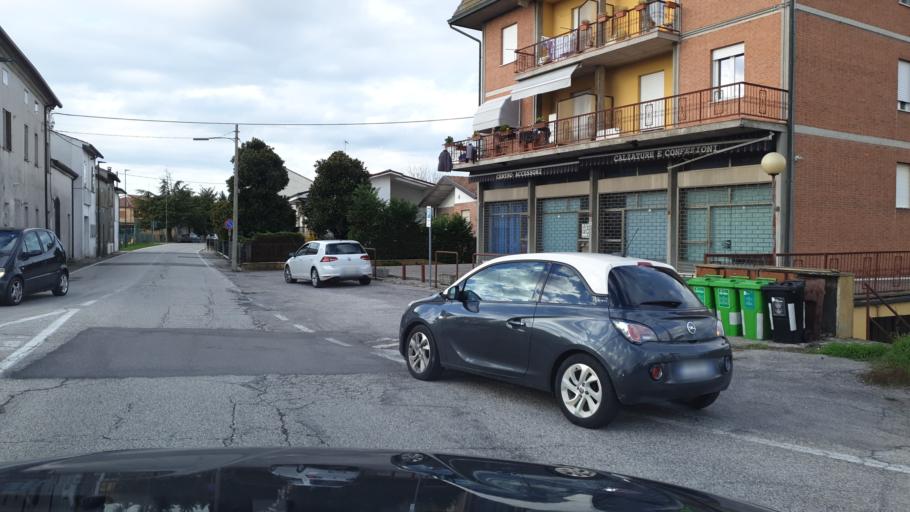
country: IT
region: Veneto
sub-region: Provincia di Rovigo
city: Villanova del Ghebbo Canton
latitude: 45.0526
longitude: 11.6468
